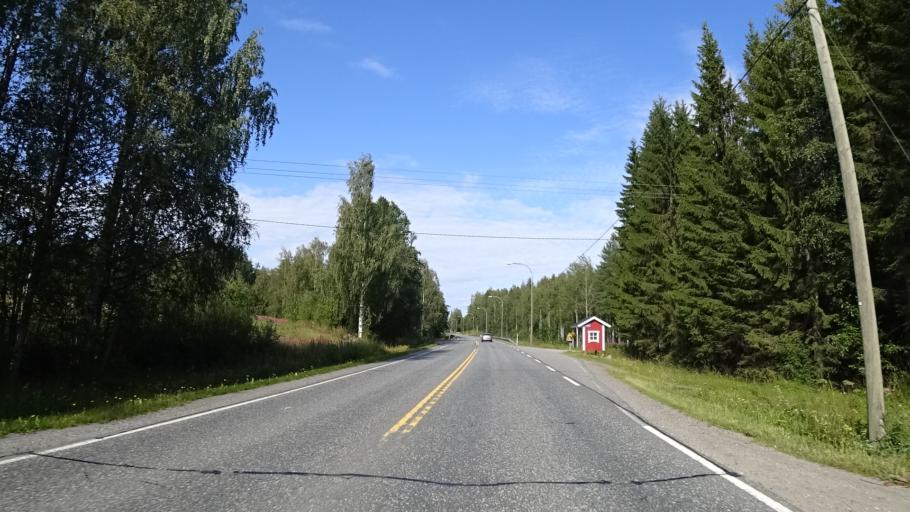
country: FI
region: North Karelia
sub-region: Joensuu
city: Eno
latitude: 62.7840
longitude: 30.0773
